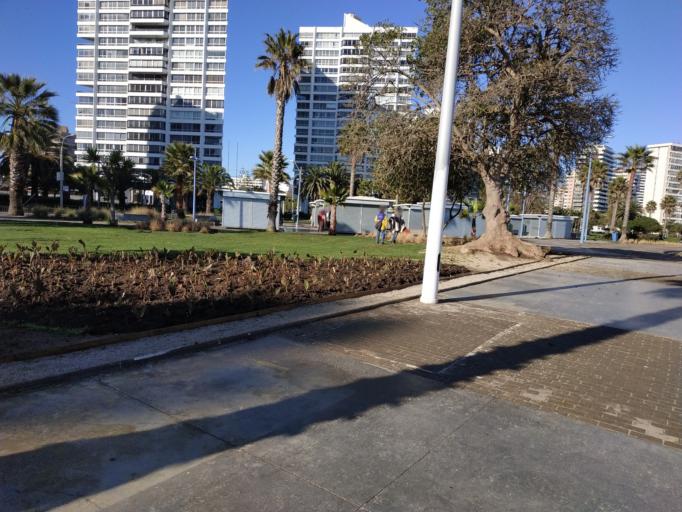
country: CL
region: Valparaiso
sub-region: Provincia de Valparaiso
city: Vina del Mar
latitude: -33.0101
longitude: -71.5527
